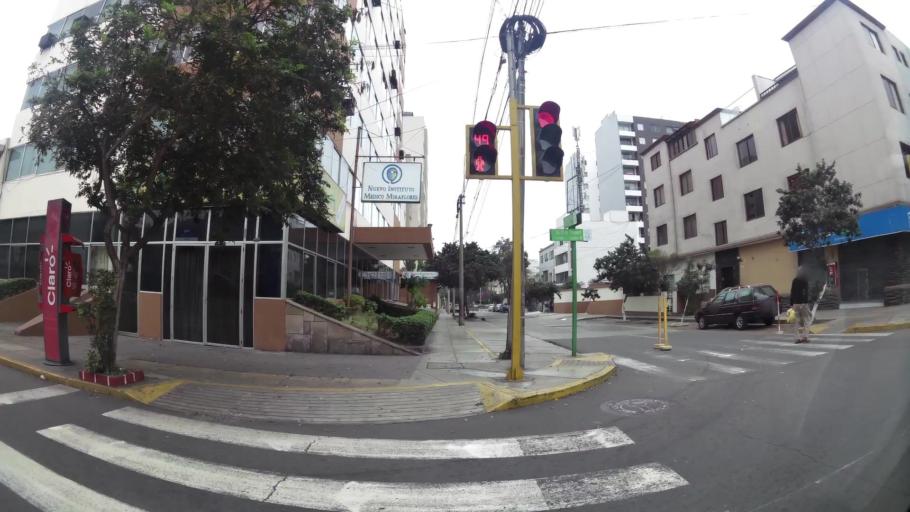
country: PE
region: Lima
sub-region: Lima
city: San Isidro
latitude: -12.1076
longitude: -77.0298
